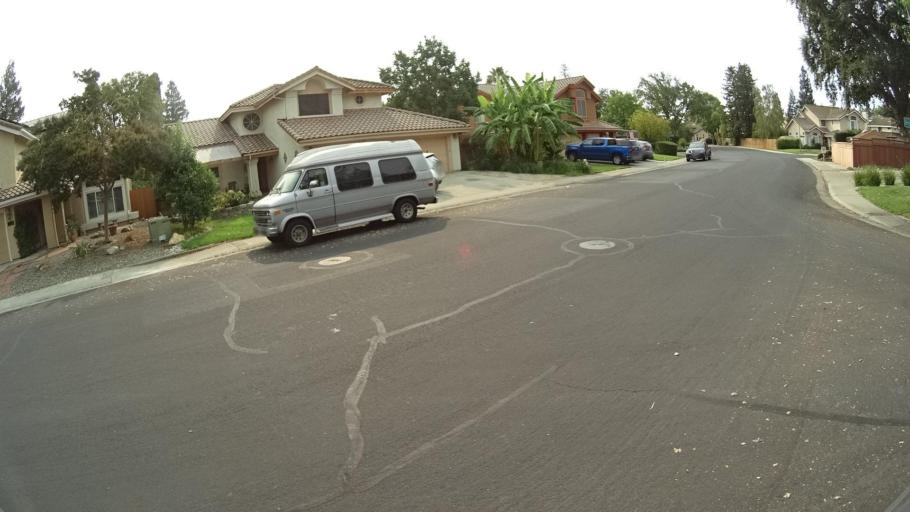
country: US
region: California
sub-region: Sacramento County
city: Laguna
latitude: 38.4157
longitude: -121.3978
